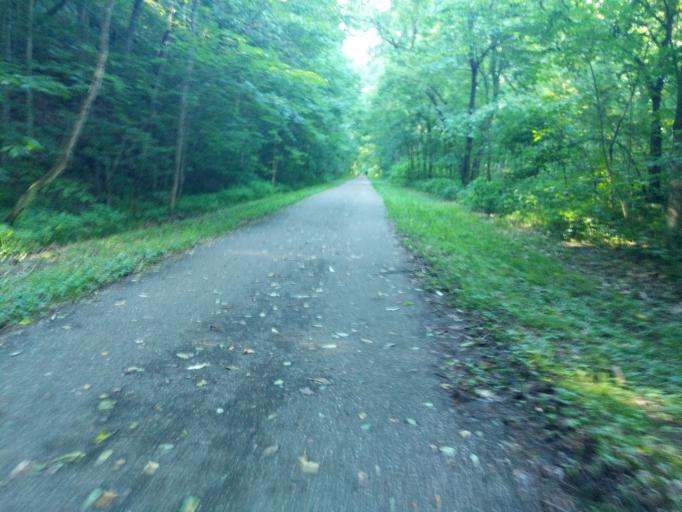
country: US
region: Ohio
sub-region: Athens County
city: Nelsonville
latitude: 39.4183
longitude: -82.1949
